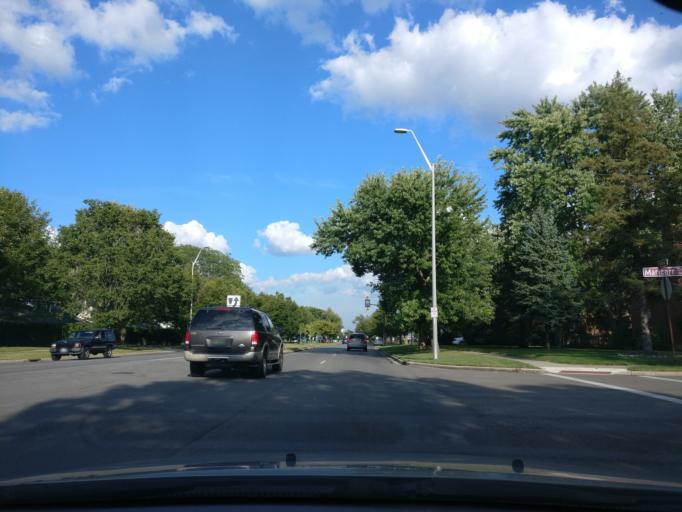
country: US
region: Ohio
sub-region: Montgomery County
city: Kettering
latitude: 39.6891
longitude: -84.1575
